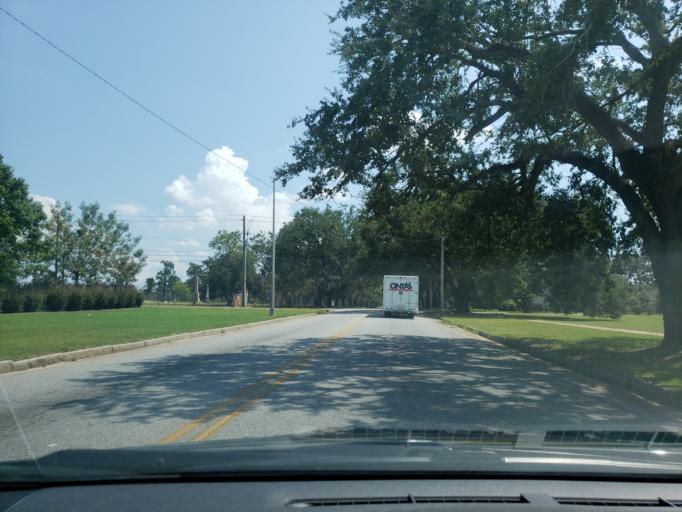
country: US
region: Georgia
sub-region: Dougherty County
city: Albany
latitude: 31.5721
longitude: -84.1537
